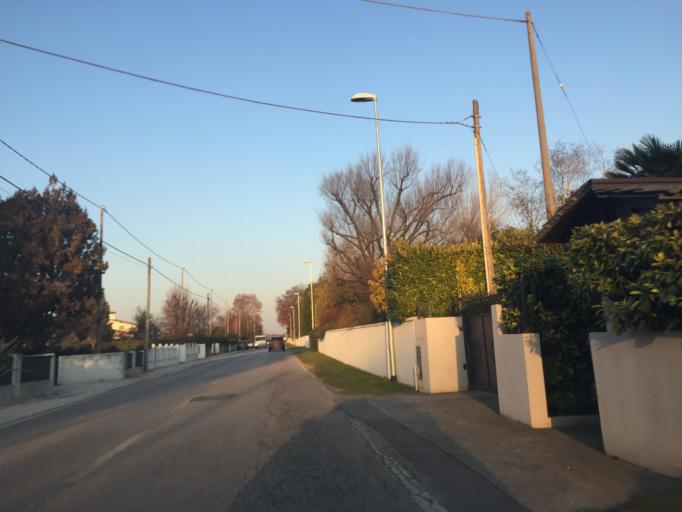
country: IT
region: Friuli Venezia Giulia
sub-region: Provincia di Pordenone
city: Vigonovo-Fontanafredda
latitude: 45.9944
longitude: 12.5529
